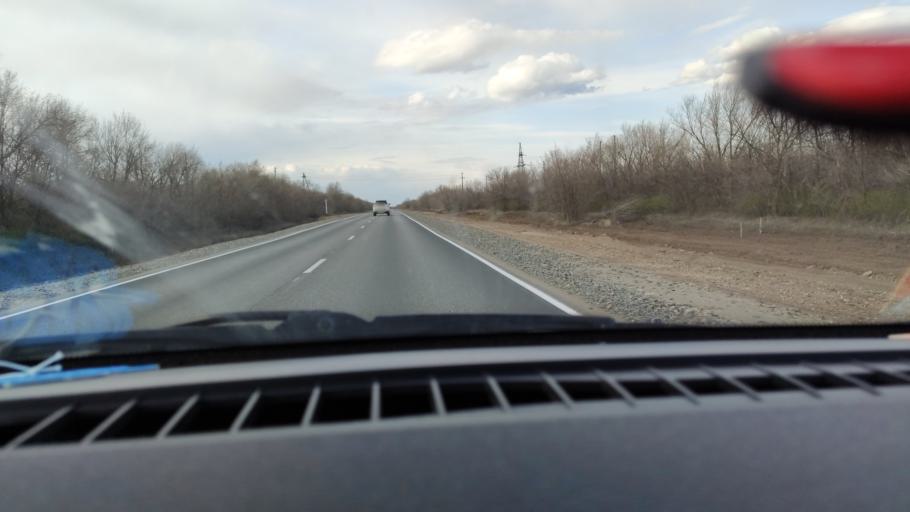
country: RU
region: Saratov
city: Krasnoarmeysk
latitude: 51.1359
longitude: 45.9598
